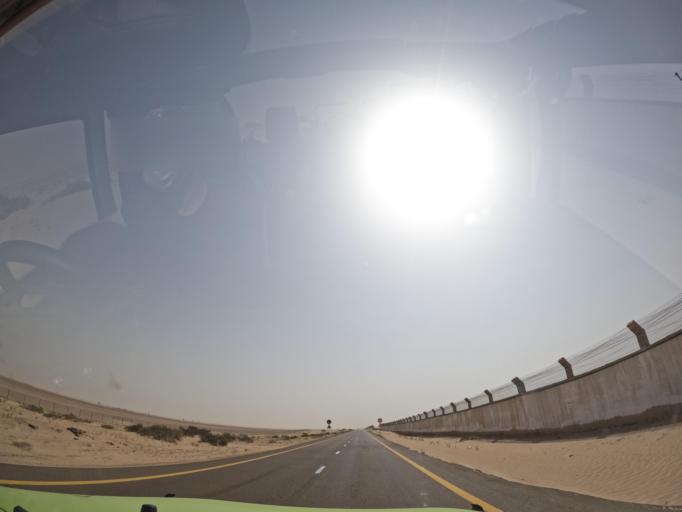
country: AE
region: Dubai
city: Dubai
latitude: 24.6150
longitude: 55.3238
